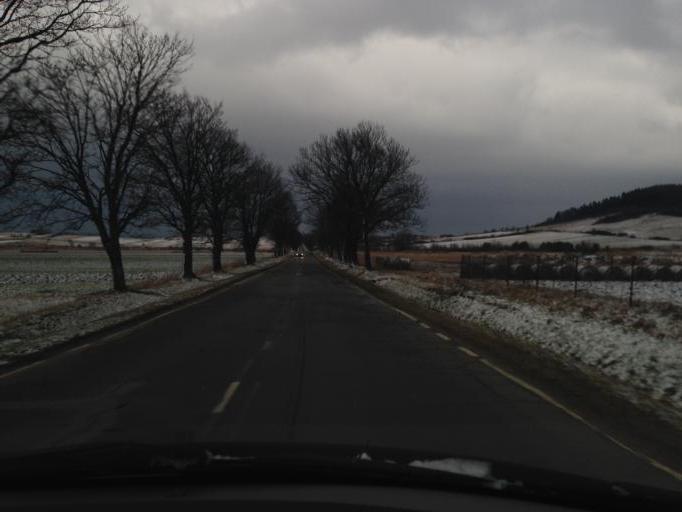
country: PL
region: Subcarpathian Voivodeship
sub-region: Powiat jasielski
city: Osiek Jasielski
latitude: 49.6111
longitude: 21.4819
